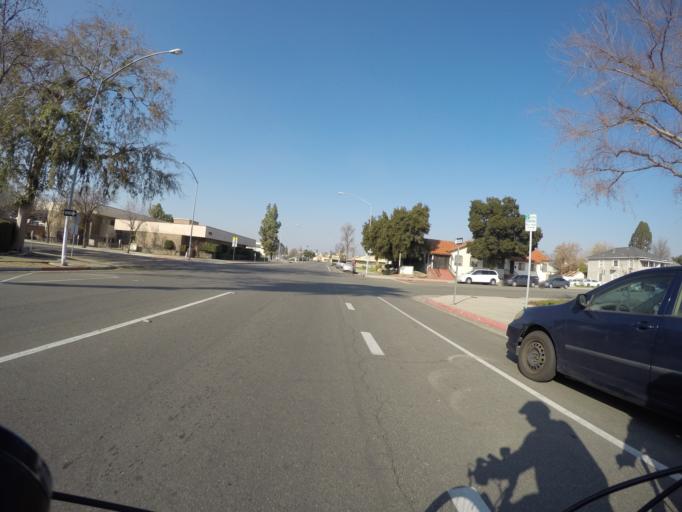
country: US
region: California
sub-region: Fresno County
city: Fresno
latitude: 36.7411
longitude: -119.7870
